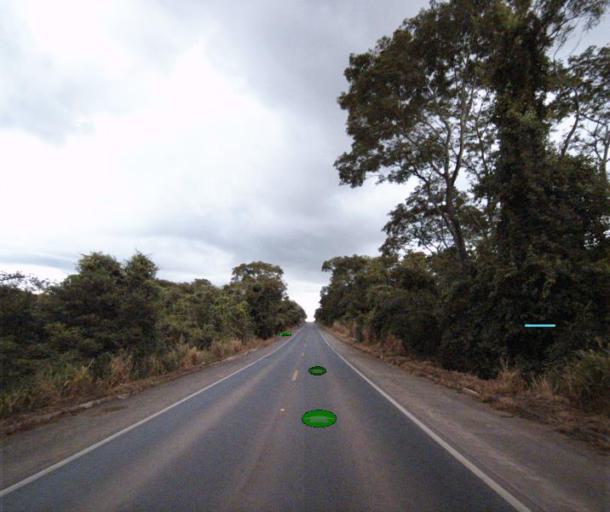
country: BR
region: Goias
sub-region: Uruacu
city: Uruacu
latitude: -14.6903
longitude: -49.2120
